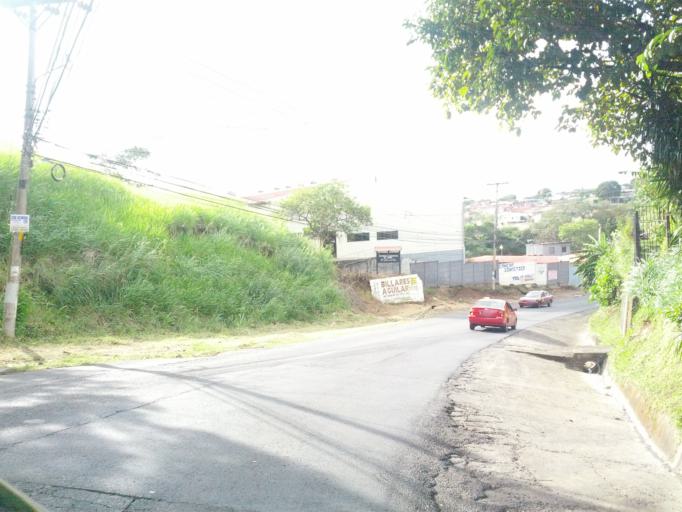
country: CR
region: Alajuela
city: Alajuela
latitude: 10.0179
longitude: -84.1962
